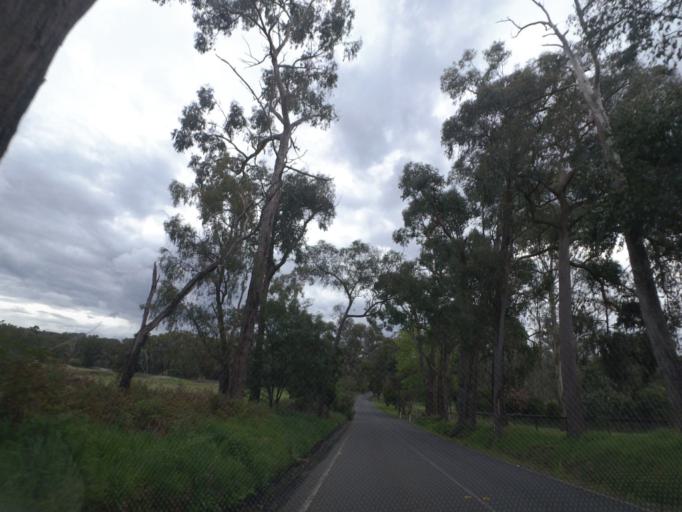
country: AU
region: Victoria
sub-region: Yarra Ranges
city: Mount Evelyn
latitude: -37.7689
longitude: 145.4286
